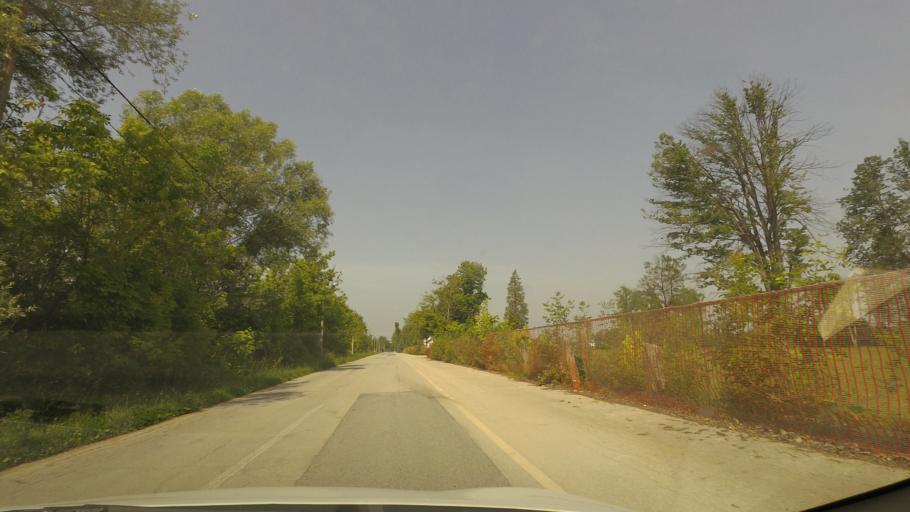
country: HR
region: Karlovacka
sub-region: Grad Karlovac
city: Karlovac
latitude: 45.4826
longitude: 15.5861
